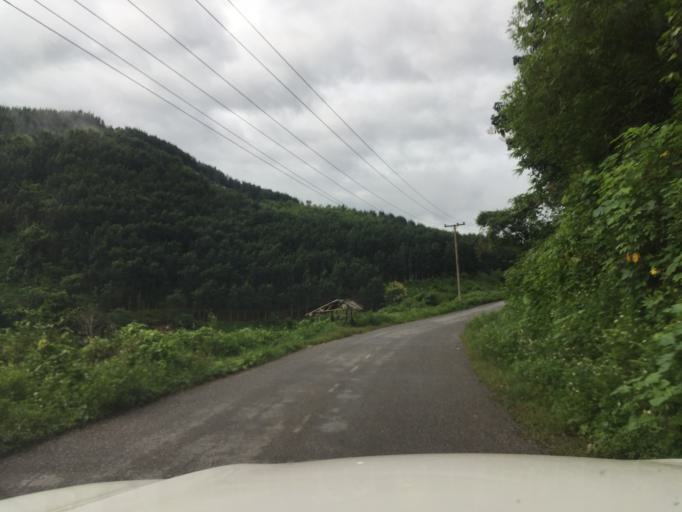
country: LA
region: Oudomxai
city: Muang La
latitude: 21.0761
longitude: 102.2439
